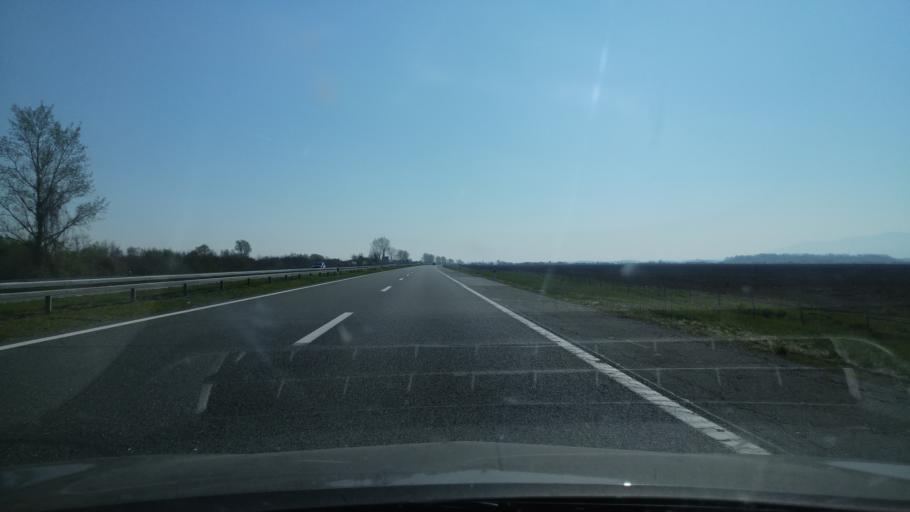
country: HR
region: Brodsko-Posavska
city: Vrbova
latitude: 45.2119
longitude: 17.5410
